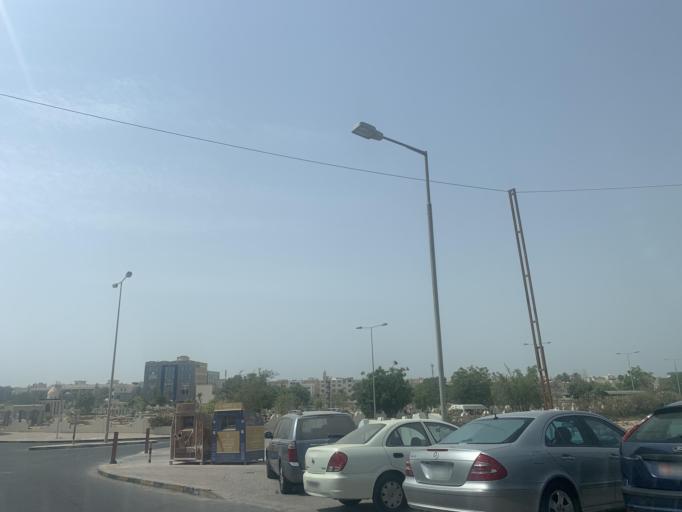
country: BH
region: Manama
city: Jidd Hafs
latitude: 26.2126
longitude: 50.4617
